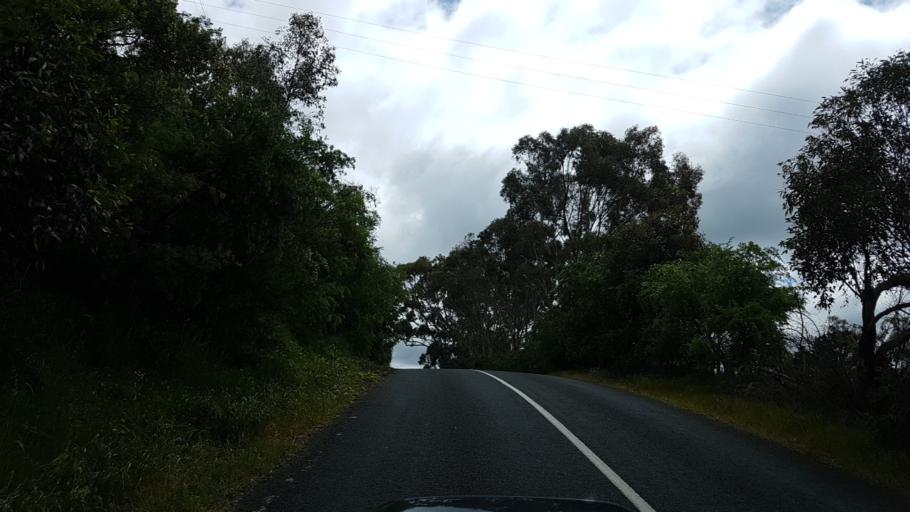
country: AU
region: South Australia
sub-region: Adelaide Hills
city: Lobethal
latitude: -34.8896
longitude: 138.8912
